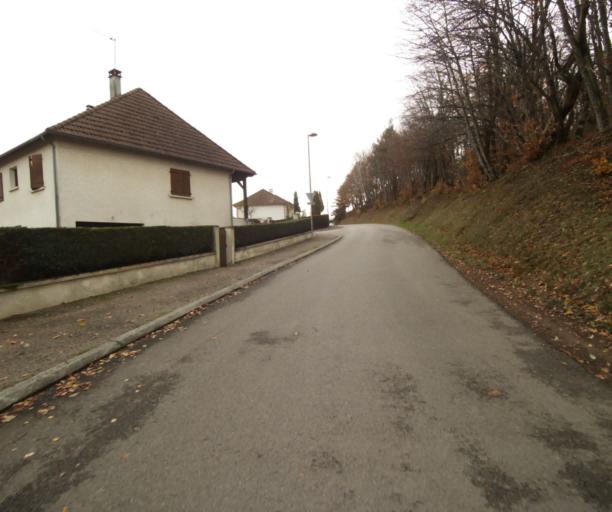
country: FR
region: Limousin
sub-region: Departement de la Correze
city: Sainte-Fortunade
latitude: 45.2175
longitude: 1.7675
